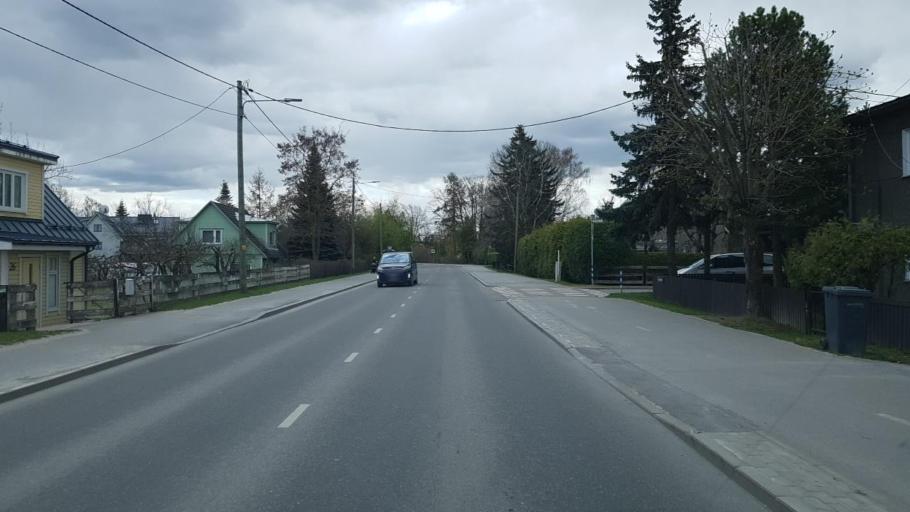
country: EE
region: Tartu
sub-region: Tartu linn
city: Tartu
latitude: 58.3587
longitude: 26.7033
